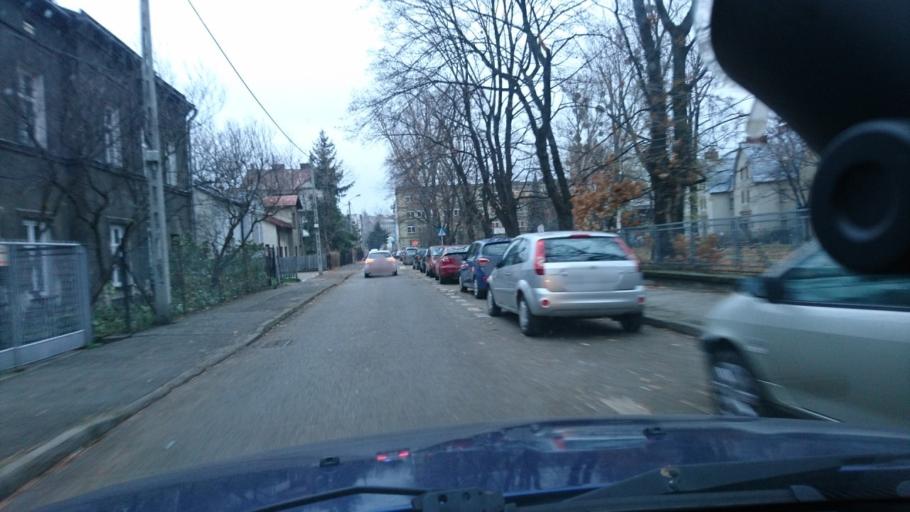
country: PL
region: Silesian Voivodeship
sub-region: Bielsko-Biala
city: Bielsko-Biala
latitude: 49.8169
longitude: 19.0504
